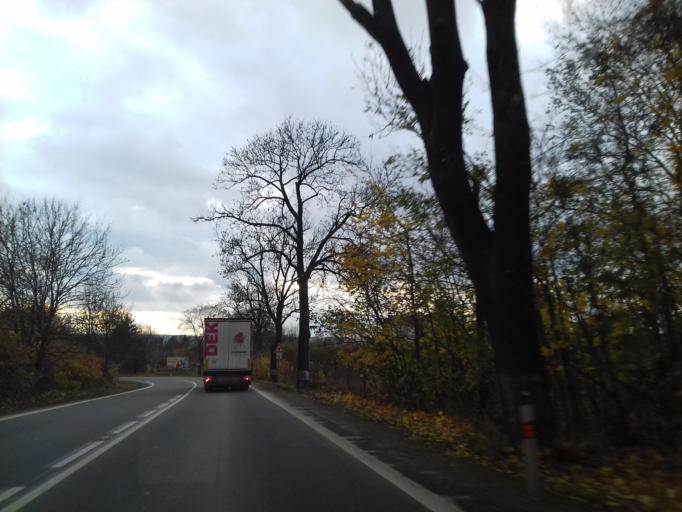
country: CZ
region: Pardubicky
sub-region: Okres Svitavy
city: Svitavy
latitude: 49.7586
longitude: 16.4888
